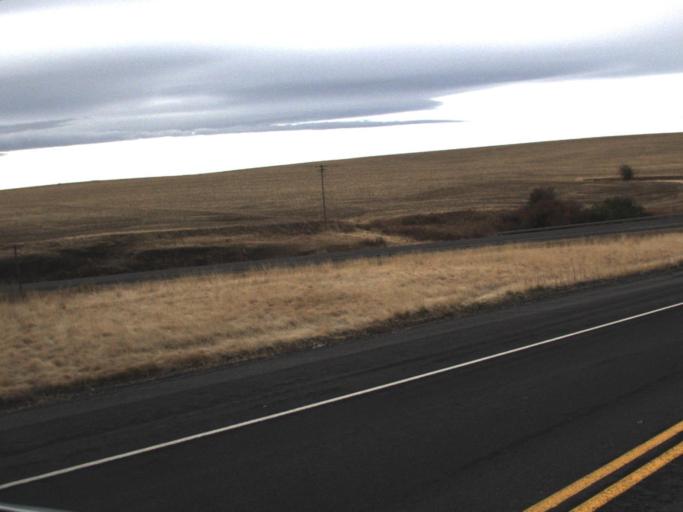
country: US
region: Washington
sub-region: Asotin County
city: Clarkston
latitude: 46.4742
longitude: -117.0426
